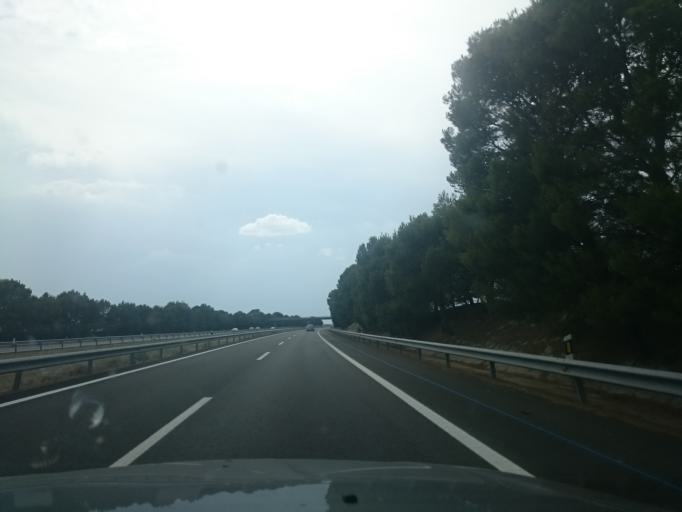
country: ES
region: Aragon
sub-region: Provincia de Zaragoza
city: Bujaraloz
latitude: 41.5192
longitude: -0.2149
